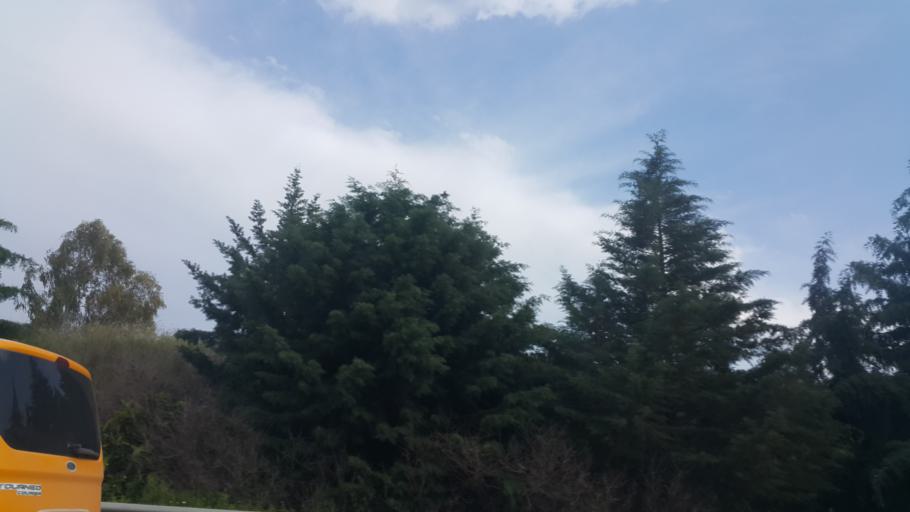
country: TR
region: Mersin
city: Kazanli
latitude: 36.9138
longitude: 34.6859
